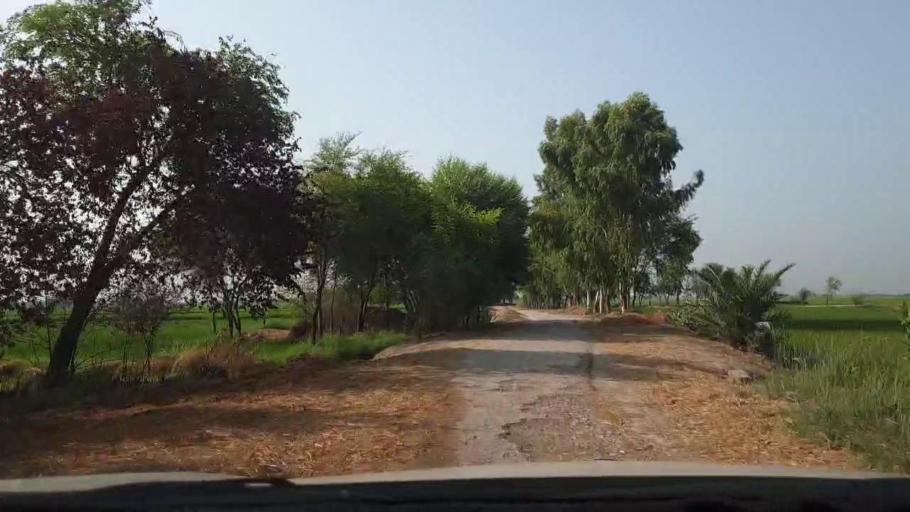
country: PK
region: Sindh
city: Goth Garelo
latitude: 27.4868
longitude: 68.1161
